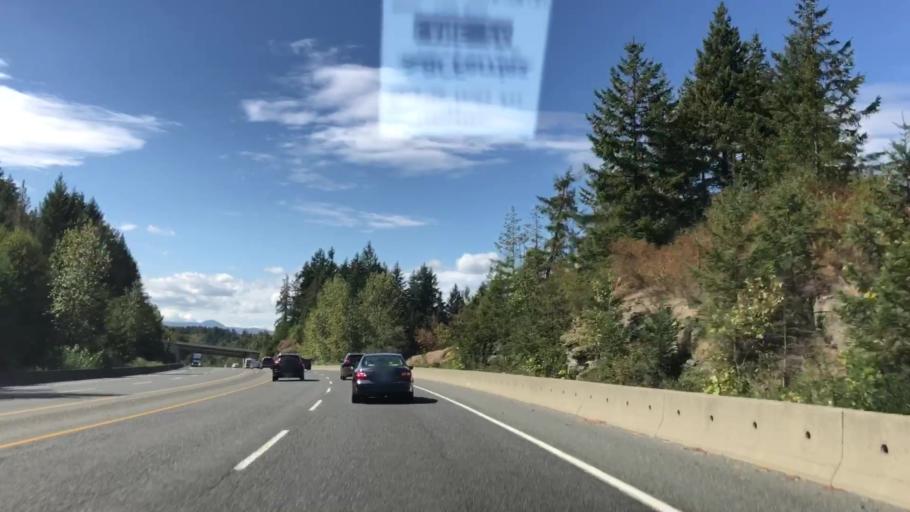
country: CA
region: British Columbia
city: Nanaimo
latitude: 49.1168
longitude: -123.8730
